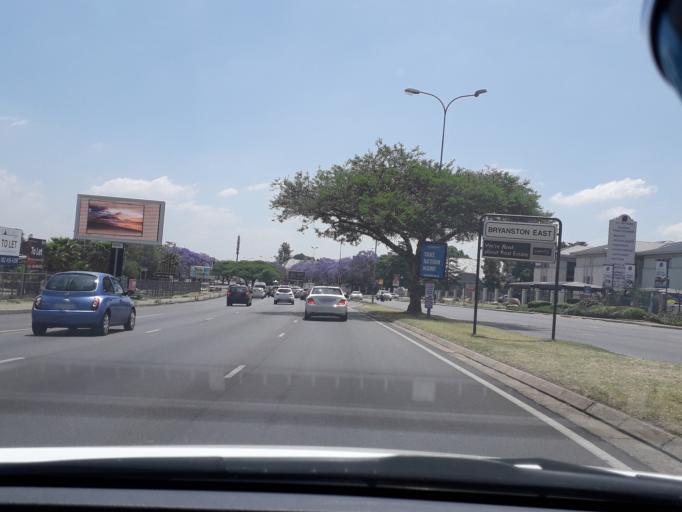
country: ZA
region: Gauteng
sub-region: City of Johannesburg Metropolitan Municipality
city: Diepsloot
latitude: -26.0490
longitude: 28.0208
